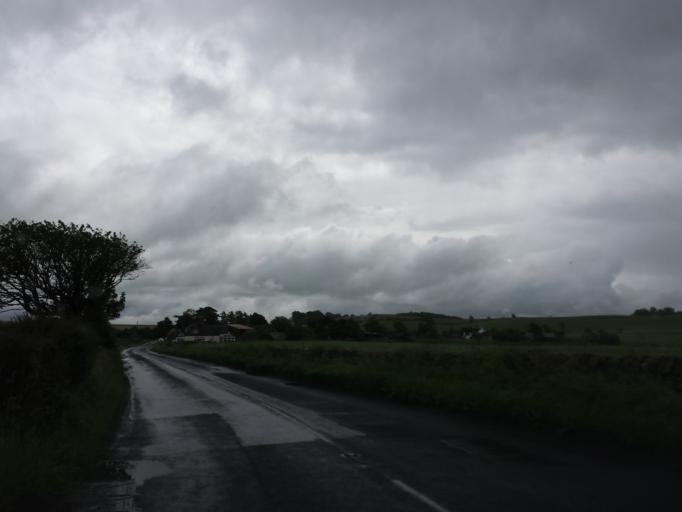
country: GB
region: Scotland
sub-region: Fife
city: Ceres
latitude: 56.2909
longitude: -2.9252
